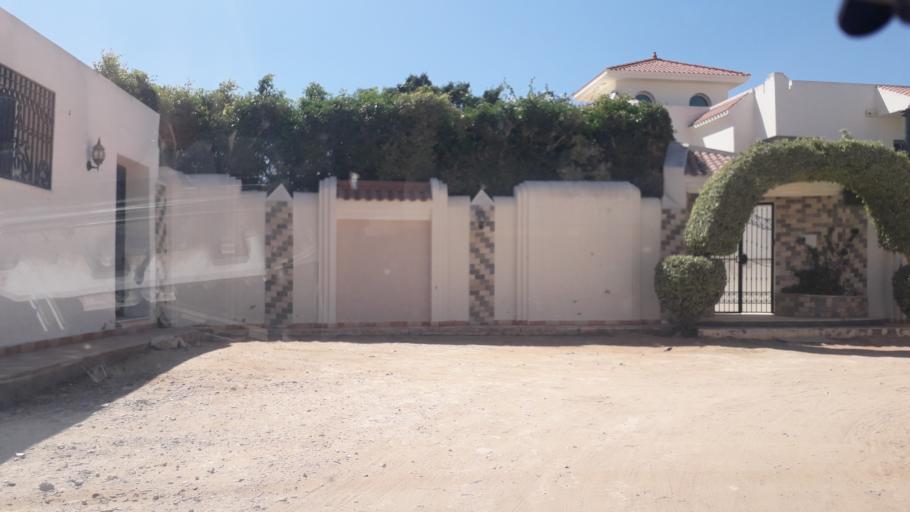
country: TN
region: Safaqis
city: Al Qarmadah
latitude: 34.8284
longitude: 10.7680
